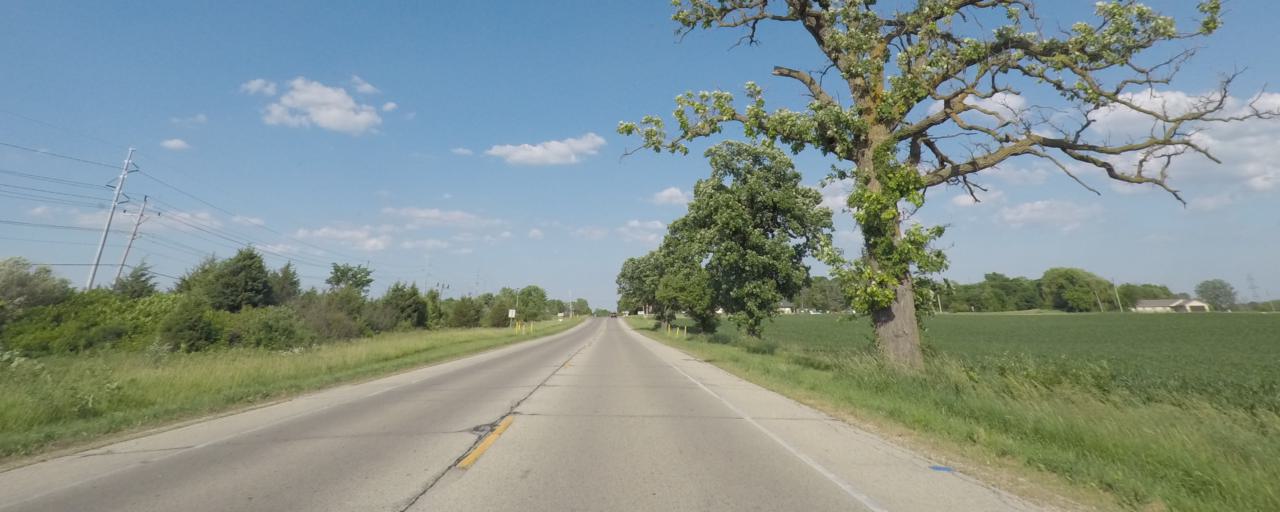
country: US
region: Wisconsin
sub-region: Waukesha County
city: Big Bend
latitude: 42.8877
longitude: -88.1888
